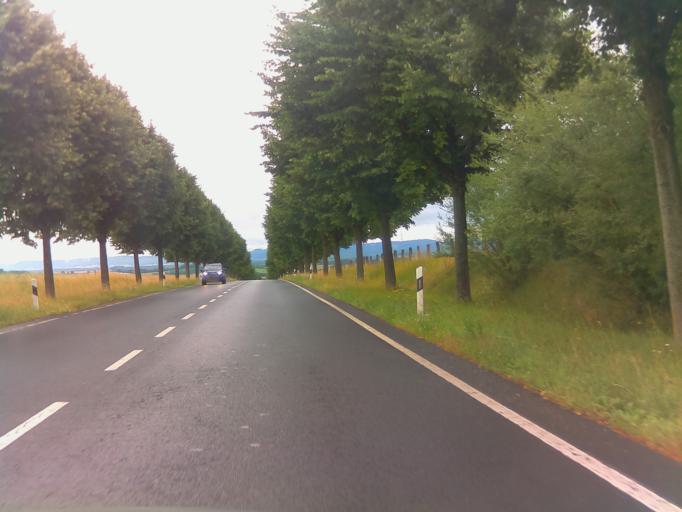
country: LU
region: Grevenmacher
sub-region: Canton de Remich
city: Dalheim
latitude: 49.5312
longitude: 6.2426
